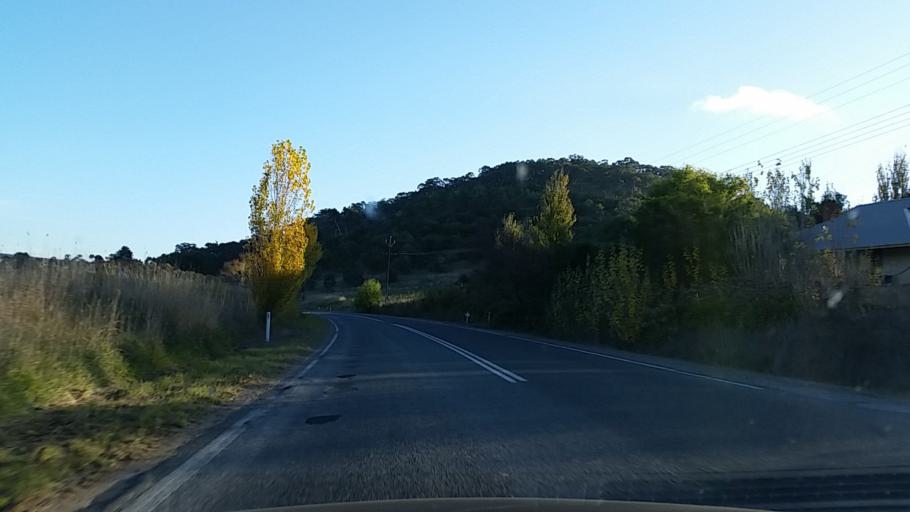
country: AU
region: South Australia
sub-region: Alexandrina
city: Mount Compass
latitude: -35.3408
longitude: 138.6517
